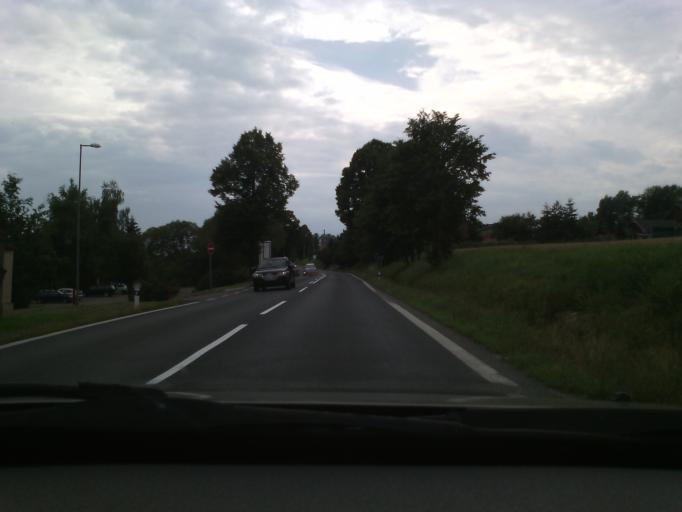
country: SK
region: Presovsky
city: Spisska Bela
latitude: 49.1704
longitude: 20.4508
